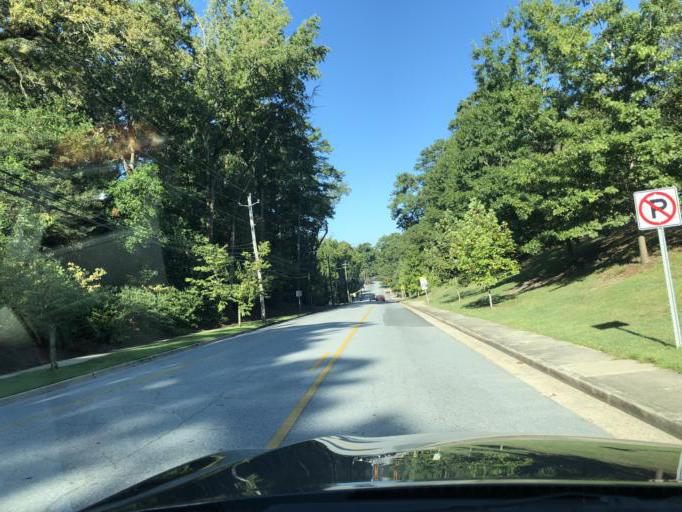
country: US
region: Georgia
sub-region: Muscogee County
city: Columbus
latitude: 32.4786
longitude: -84.9627
